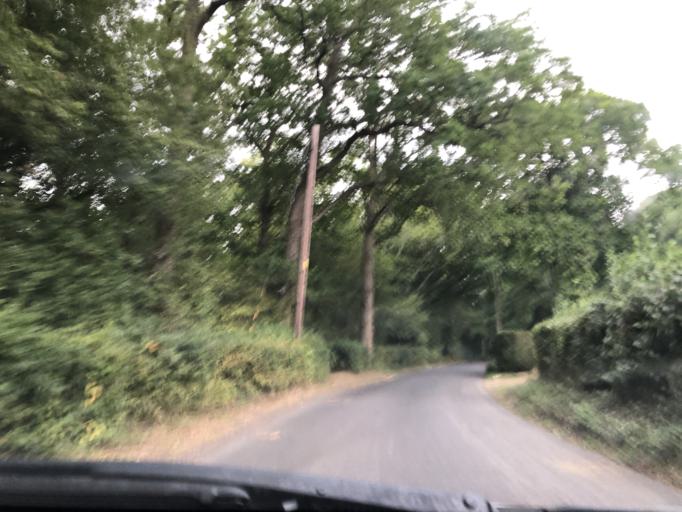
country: GB
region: England
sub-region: Kent
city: Sevenoaks
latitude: 51.2385
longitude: 0.2346
